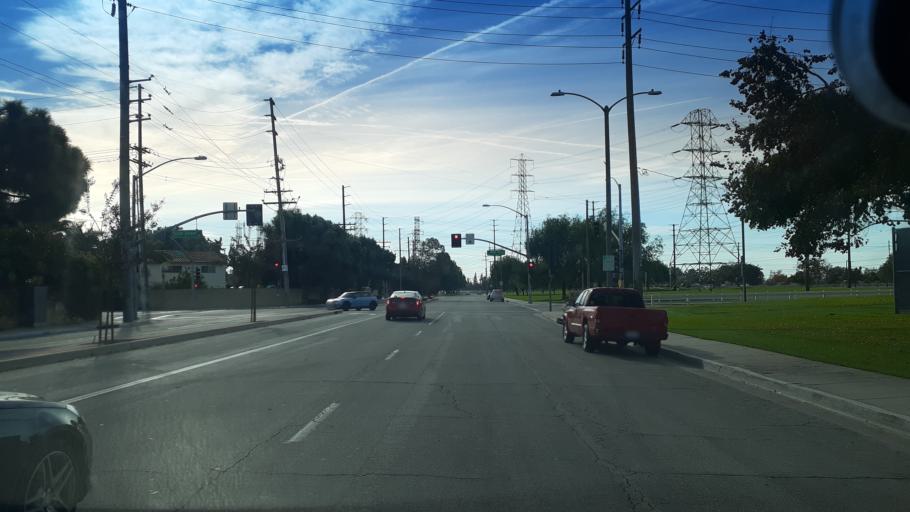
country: US
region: California
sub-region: Los Angeles County
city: Artesia
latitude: 33.8540
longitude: -118.0996
